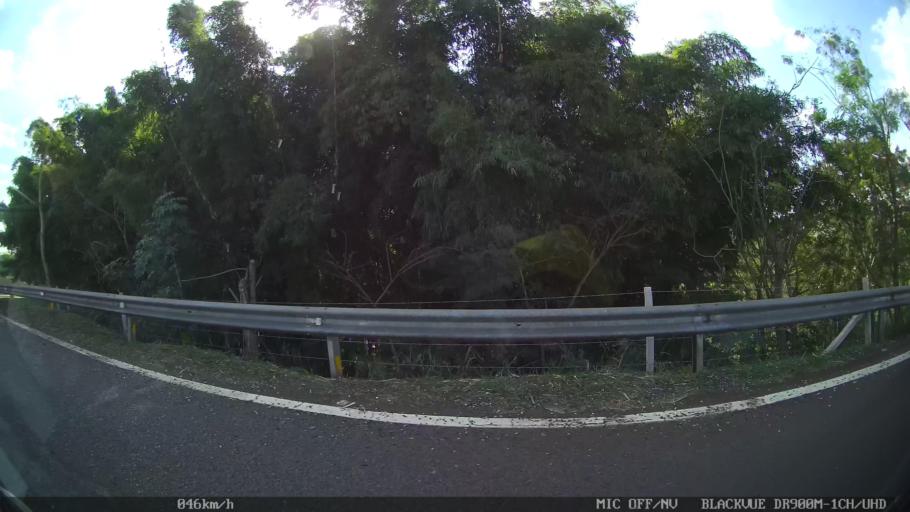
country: BR
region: Sao Paulo
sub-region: Ribeirao Preto
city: Ribeirao Preto
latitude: -21.1973
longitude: -47.8764
